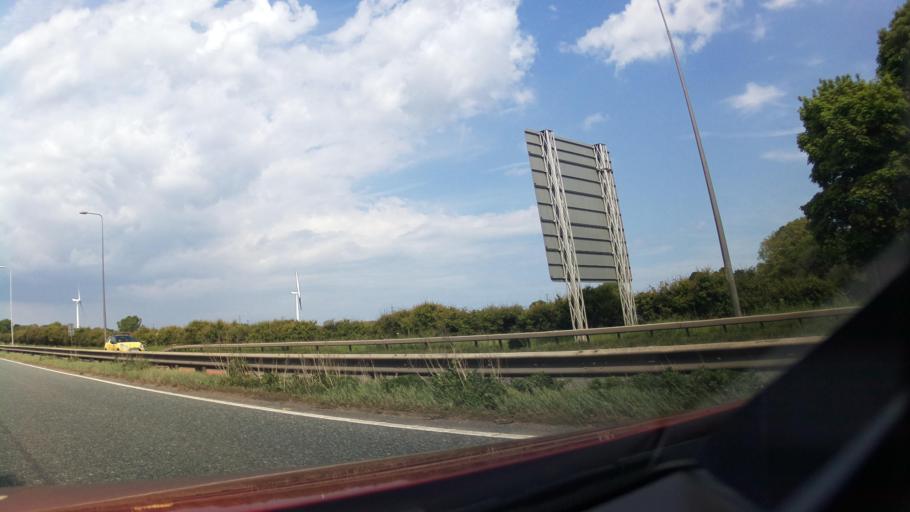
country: GB
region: England
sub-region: Hartlepool
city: Elwick
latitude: 54.6821
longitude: -1.3023
